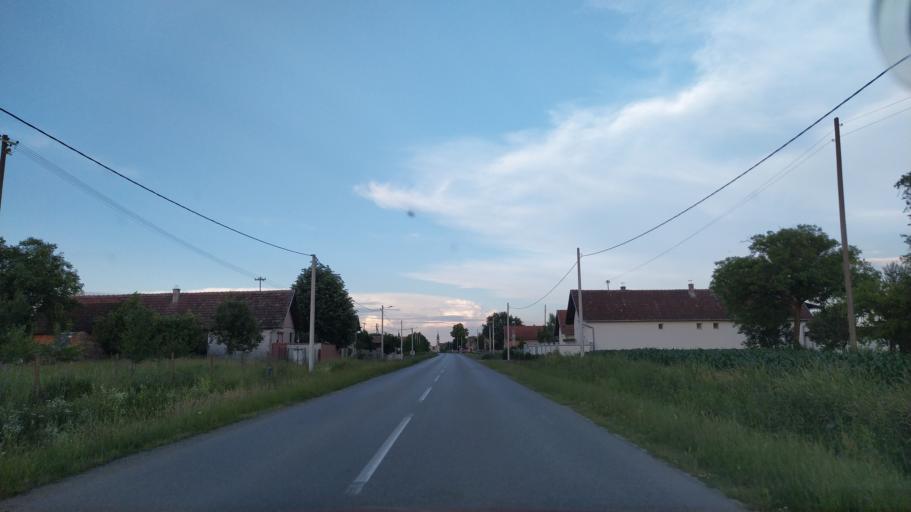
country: HR
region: Osjecko-Baranjska
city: Gorjani
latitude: 45.4607
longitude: 18.3115
